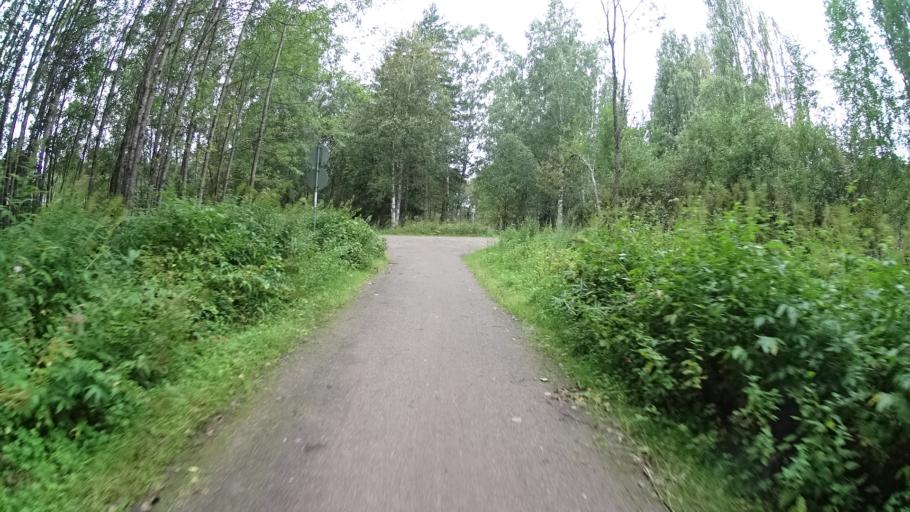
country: FI
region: Uusimaa
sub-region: Helsinki
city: Teekkarikylae
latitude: 60.2692
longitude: 24.8929
